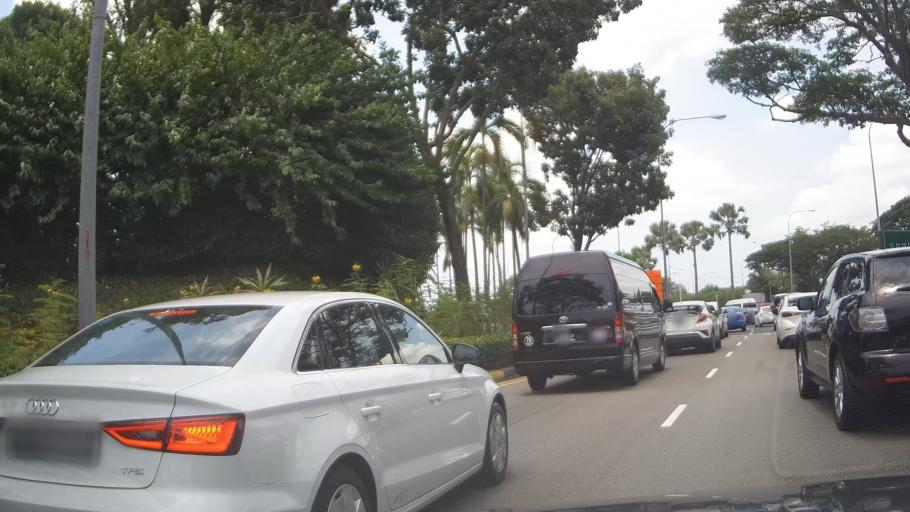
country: SG
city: Singapore
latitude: 1.3497
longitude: 103.9858
